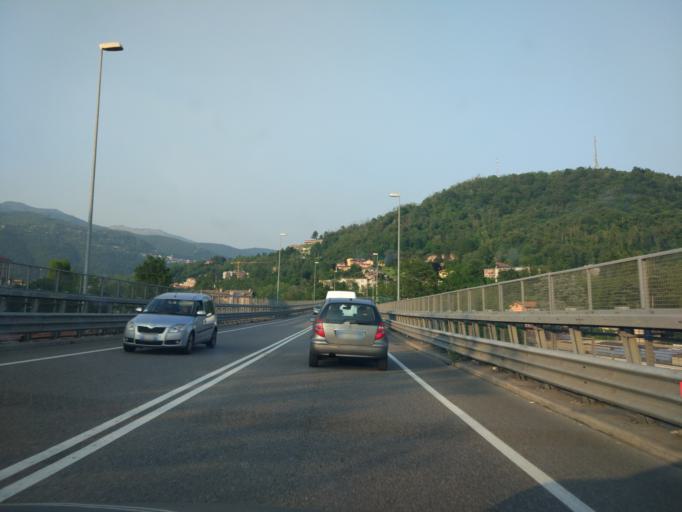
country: IT
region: Lombardy
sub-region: Provincia di Como
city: Como
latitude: 45.7880
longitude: 9.0873
